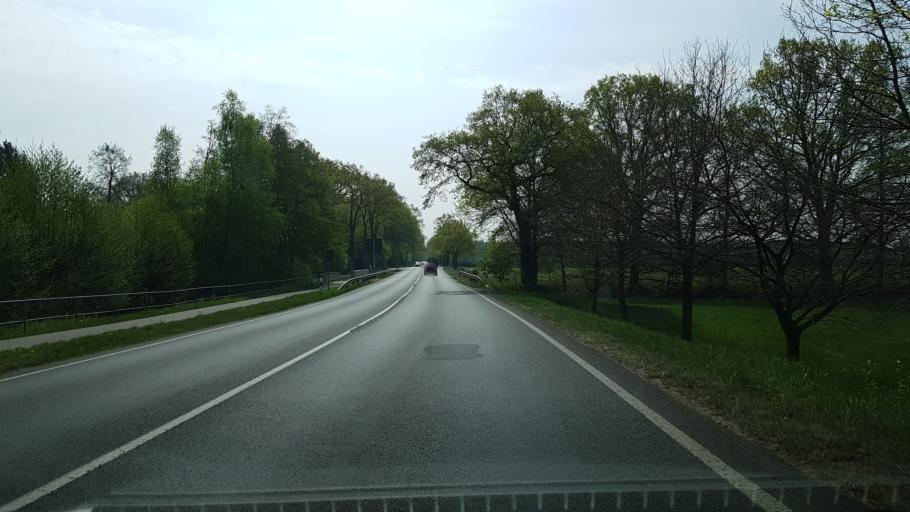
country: DE
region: Lower Saxony
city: Soltau
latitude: 52.9680
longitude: 9.8530
